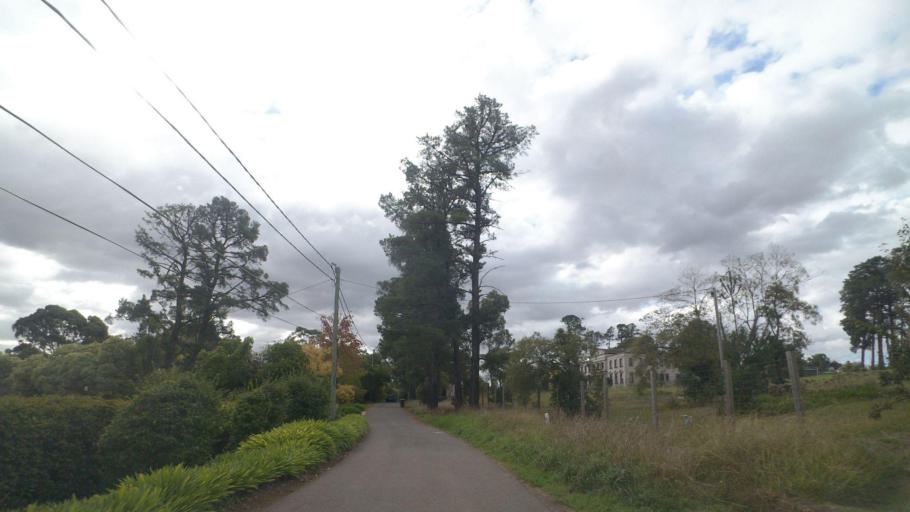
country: AU
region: Victoria
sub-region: Nillumbik
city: Eltham
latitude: -37.7570
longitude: 145.1515
